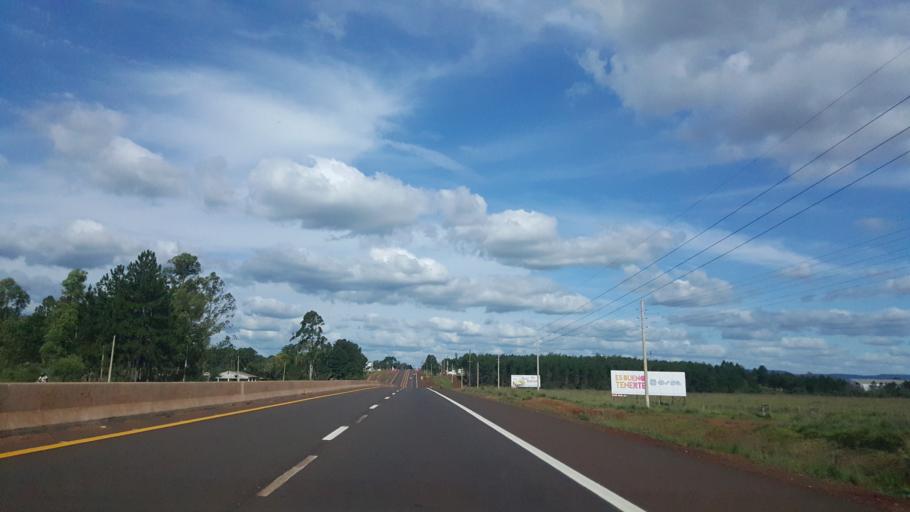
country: AR
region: Misiones
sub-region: Departamento de Candelaria
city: Candelaria
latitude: -27.4698
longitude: -55.7608
